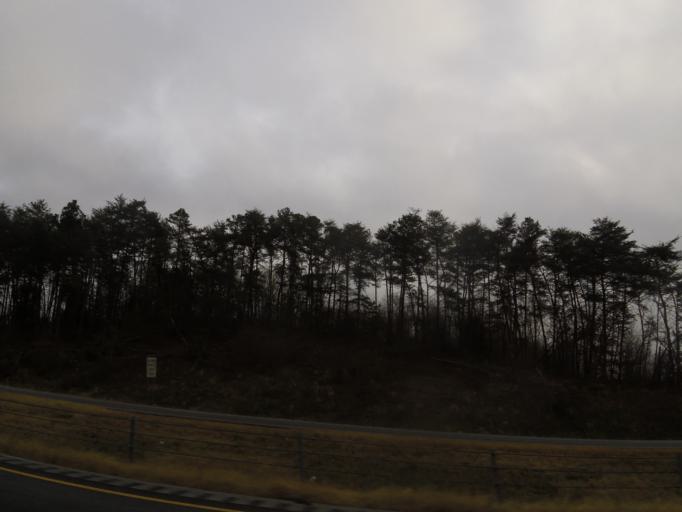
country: US
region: Alabama
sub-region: Chilton County
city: Jemison
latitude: 33.0308
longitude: -86.7214
